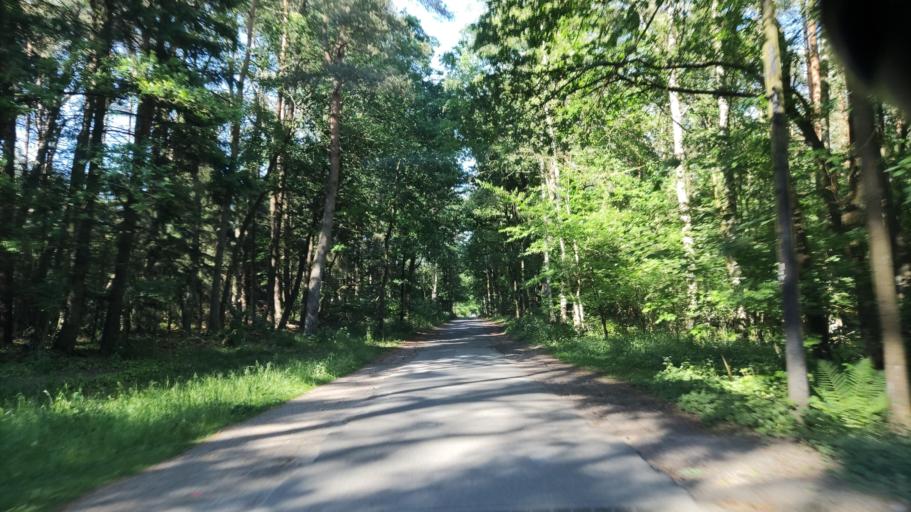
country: DE
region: Lower Saxony
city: Stelle
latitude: 53.3781
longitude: 10.0542
